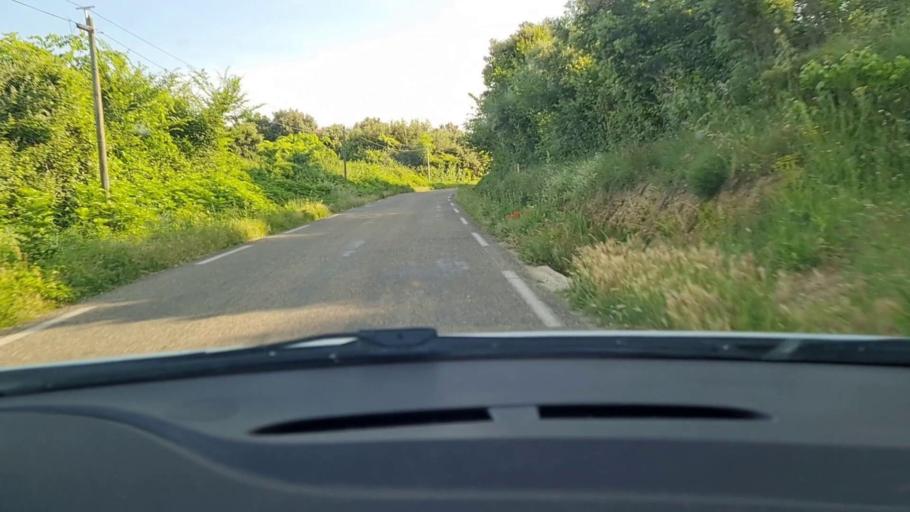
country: FR
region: Languedoc-Roussillon
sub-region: Departement du Gard
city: Bellegarde
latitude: 43.7650
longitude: 4.5109
